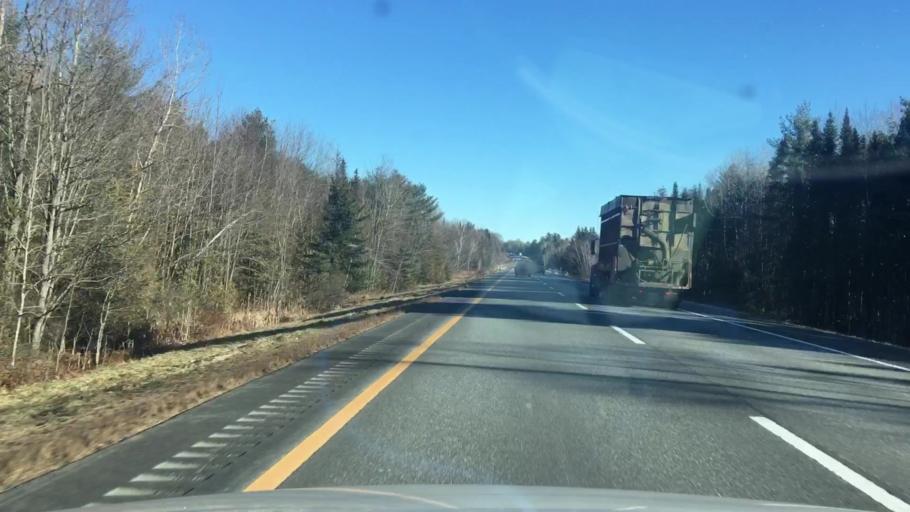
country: US
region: Maine
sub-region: Somerset County
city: Palmyra
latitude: 44.8102
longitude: -69.3543
